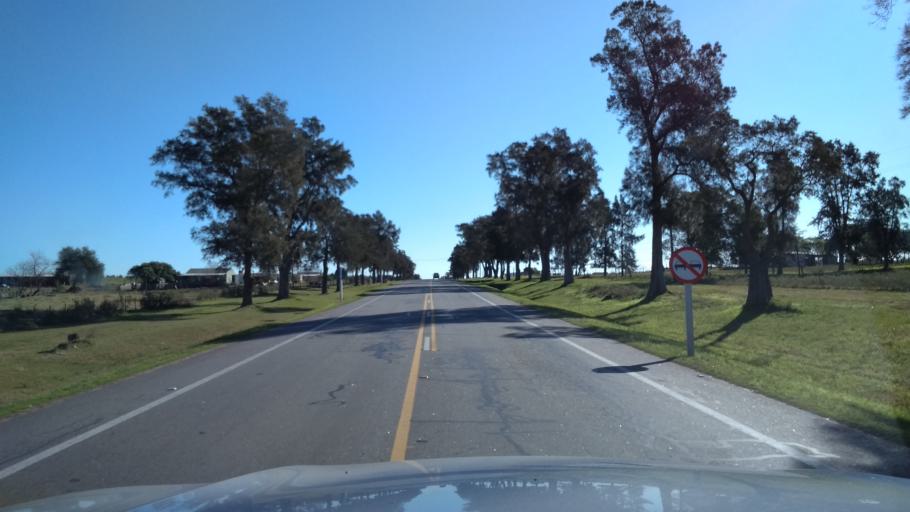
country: UY
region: Canelones
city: San Jacinto
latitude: -34.5400
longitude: -55.8965
